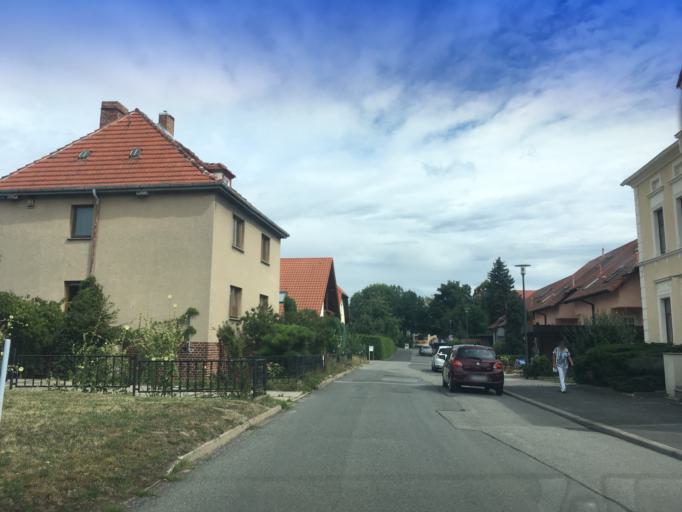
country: DE
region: Saxony
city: Goerlitz
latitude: 51.1457
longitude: 14.9496
